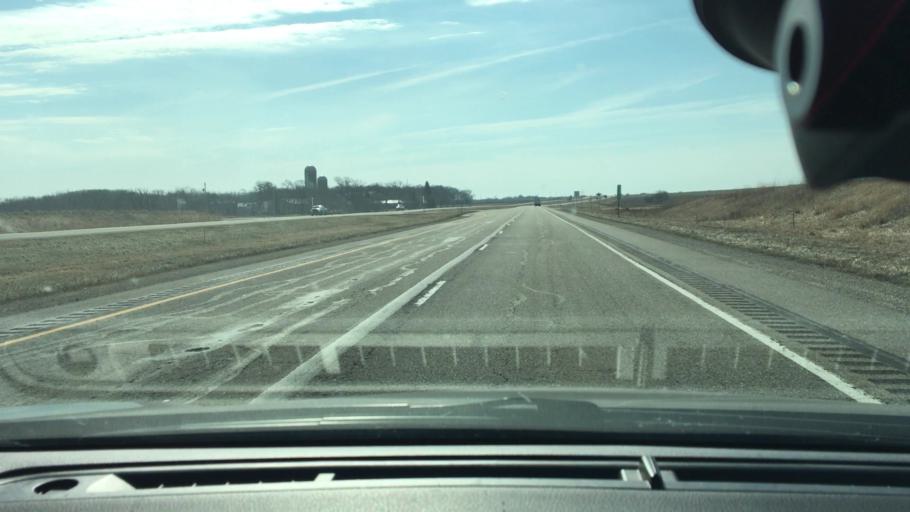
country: US
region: Iowa
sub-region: Chickasaw County
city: Nashua
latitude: 42.9966
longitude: -92.6026
